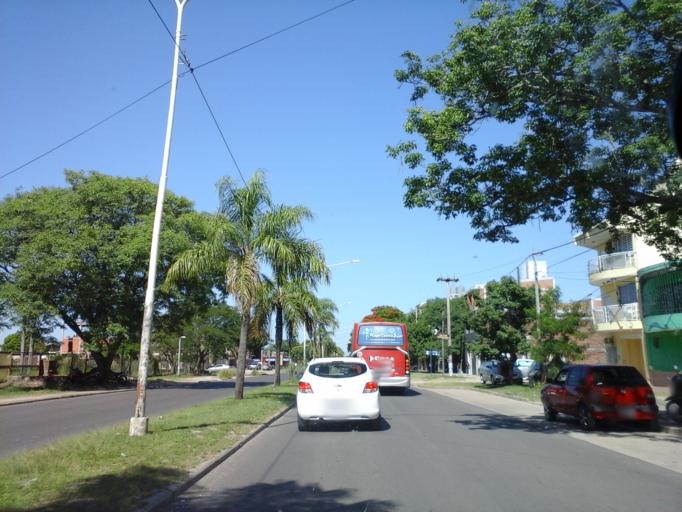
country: AR
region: Corrientes
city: Corrientes
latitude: -27.4655
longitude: -58.7852
